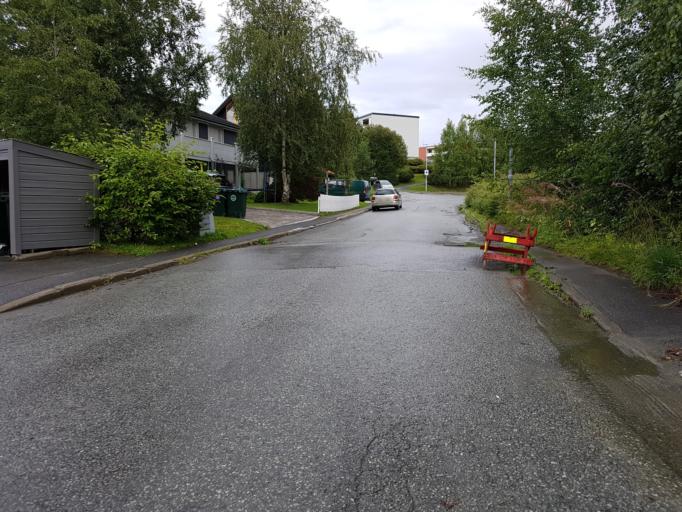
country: NO
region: Sor-Trondelag
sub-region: Trondheim
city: Trondheim
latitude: 63.4019
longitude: 10.4130
